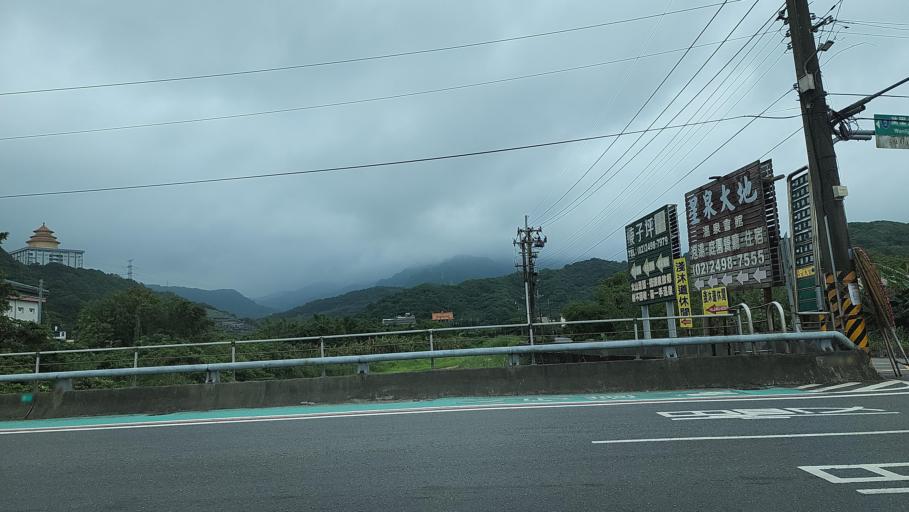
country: TW
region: Taiwan
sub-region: Keelung
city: Keelung
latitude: 25.2093
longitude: 121.6506
